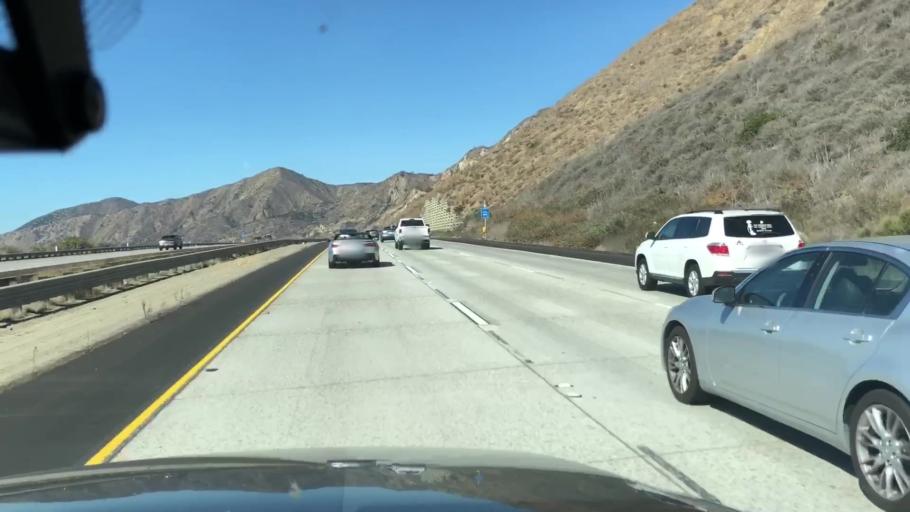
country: US
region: California
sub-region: Ventura County
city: Ventura
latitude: 34.3134
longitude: -119.3586
